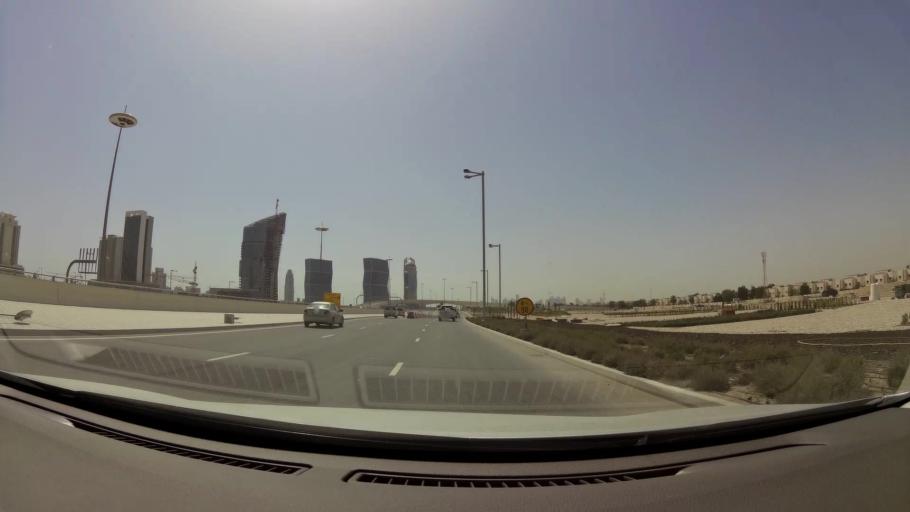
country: QA
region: Baladiyat ad Dawhah
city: Doha
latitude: 25.3870
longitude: 51.5187
